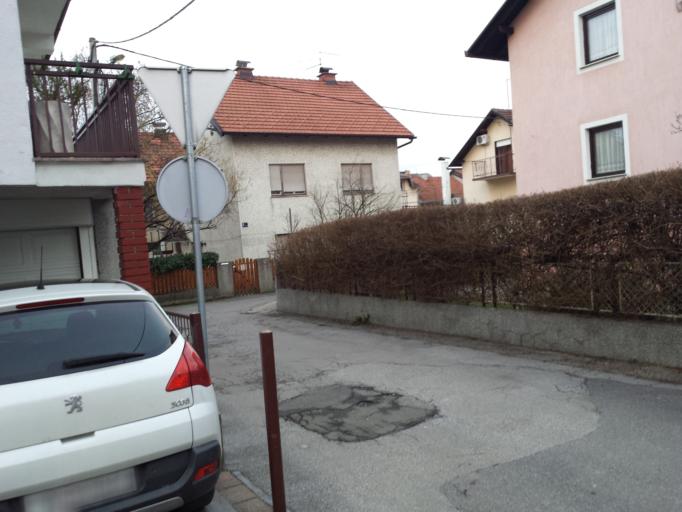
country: HR
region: Grad Zagreb
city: Jankomir
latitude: 45.7998
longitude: 15.9232
